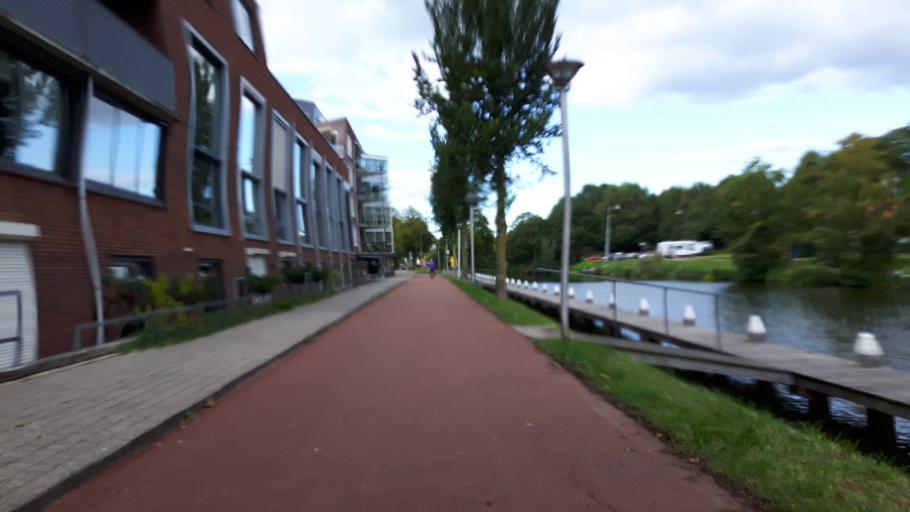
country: NL
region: Utrecht
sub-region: Gemeente Vianen
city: Vianen
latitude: 51.9905
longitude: 5.0962
